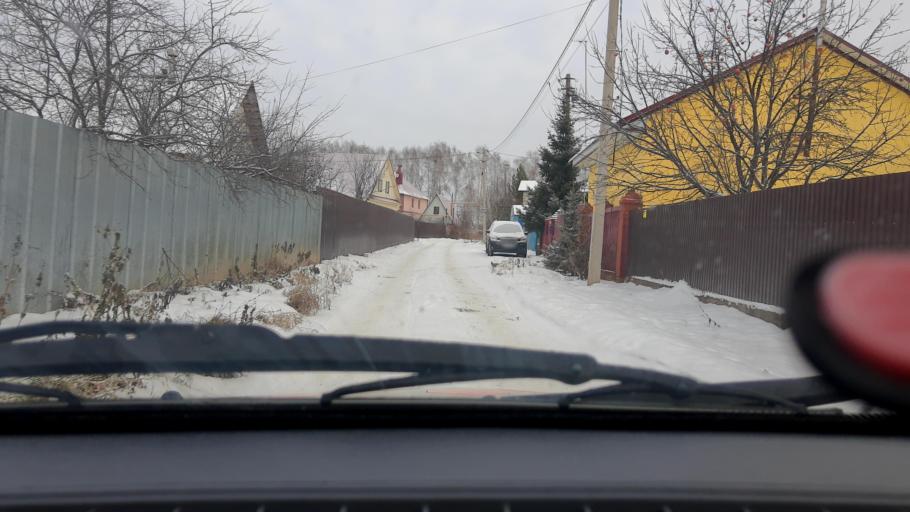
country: RU
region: Bashkortostan
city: Iglino
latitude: 54.7428
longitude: 56.2811
